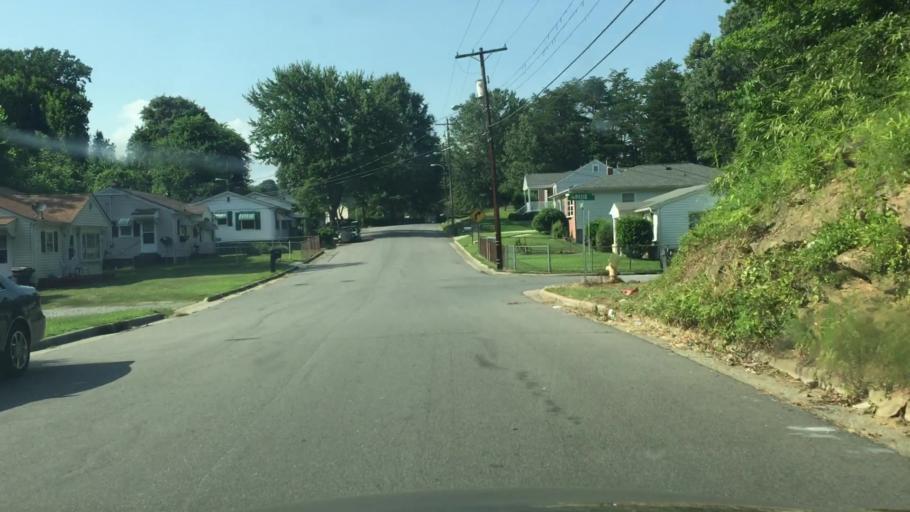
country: US
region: North Carolina
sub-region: Rockingham County
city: Reidsville
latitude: 36.3672
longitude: -79.6714
